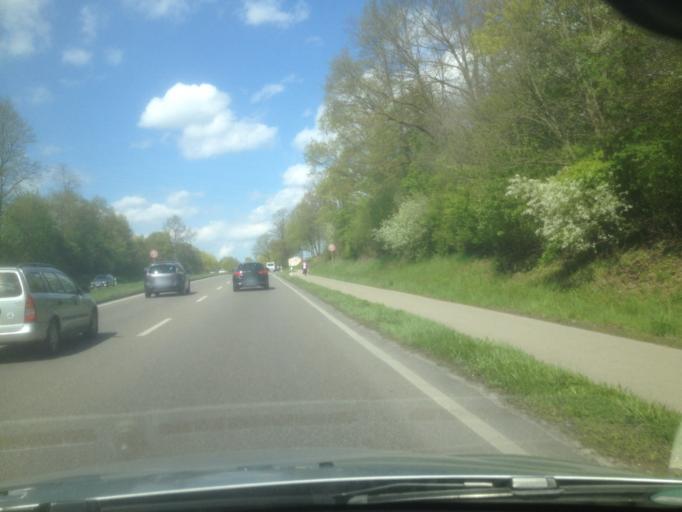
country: DE
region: Bavaria
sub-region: Swabia
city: Stadtbergen
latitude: 48.3749
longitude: 10.8474
